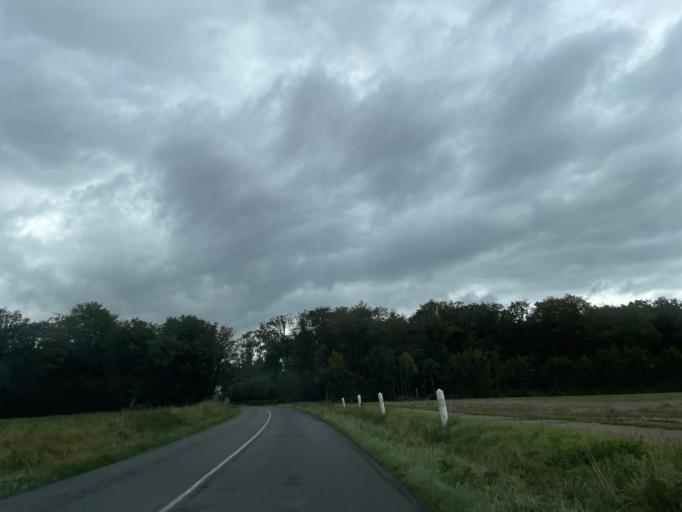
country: FR
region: Ile-de-France
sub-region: Departement de Seine-et-Marne
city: Sammeron
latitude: 48.8918
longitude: 3.0656
